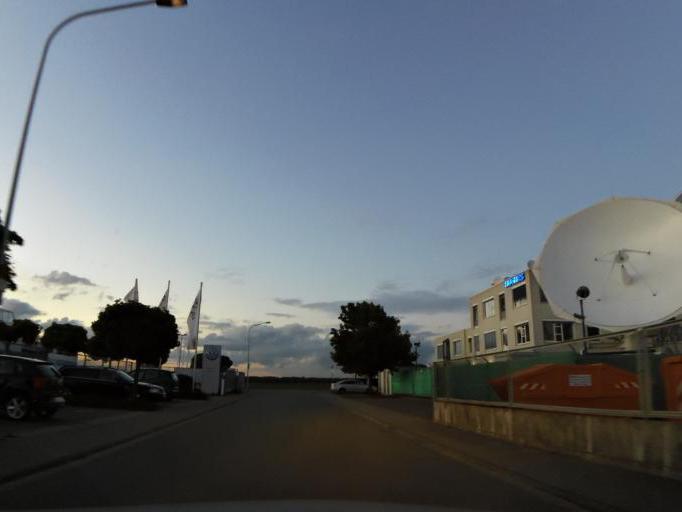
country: DE
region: Hesse
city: Griesheim
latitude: 49.8708
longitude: 8.5599
